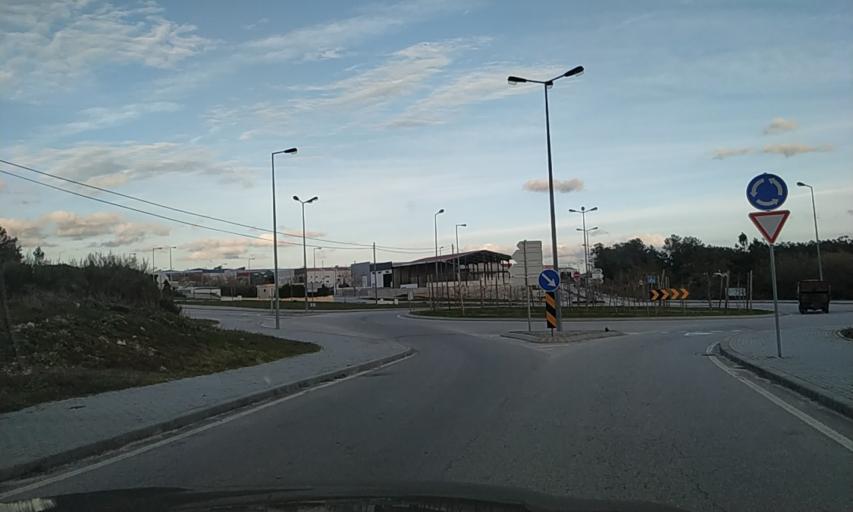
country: PT
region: Braganca
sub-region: Carrazeda de Ansiaes
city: Carrazeda de Anciaes
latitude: 41.2461
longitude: -7.3186
